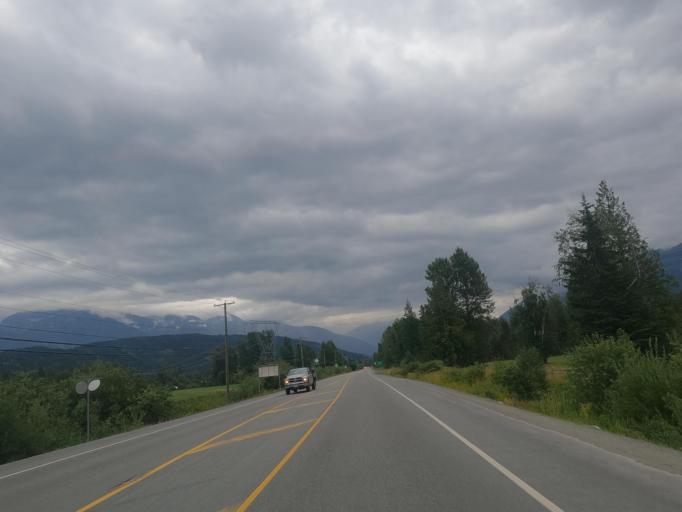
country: CA
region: British Columbia
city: Pemberton
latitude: 50.3158
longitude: -122.7917
